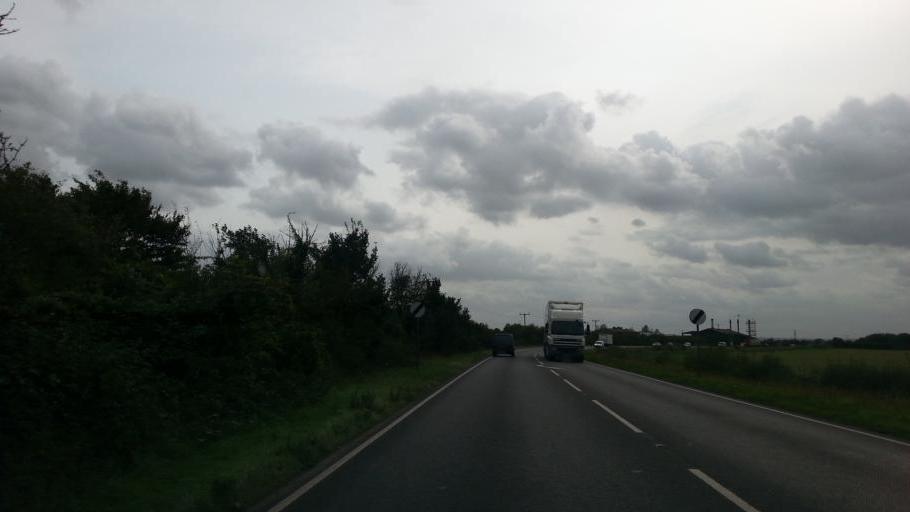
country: GB
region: England
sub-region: Cambridgeshire
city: Duxford
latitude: 52.0850
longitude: 0.1103
